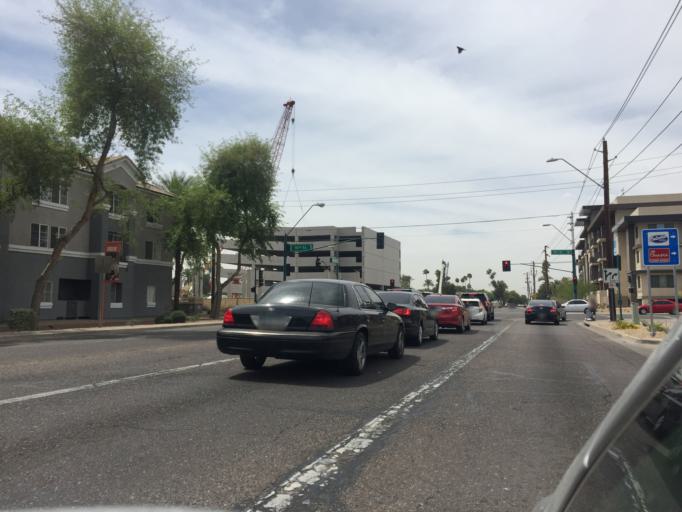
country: US
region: Arizona
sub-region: Maricopa County
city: Phoenix
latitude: 33.5056
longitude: -112.0469
